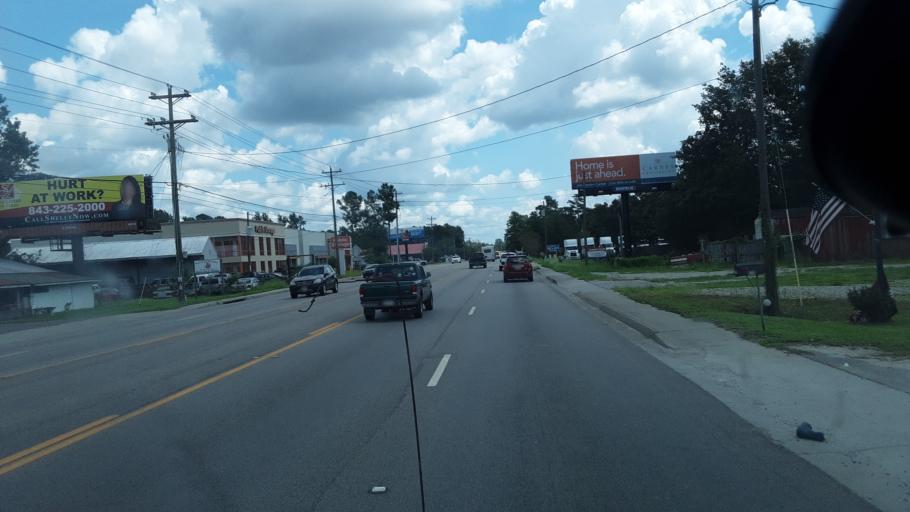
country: US
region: South Carolina
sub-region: Berkeley County
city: Sangaree
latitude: 33.0445
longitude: -80.1183
